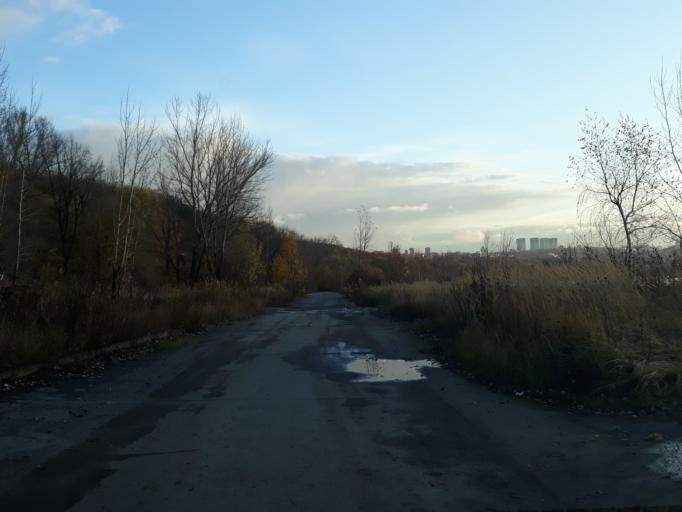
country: RU
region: Nizjnij Novgorod
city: Nizhniy Novgorod
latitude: 56.2734
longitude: 43.9699
